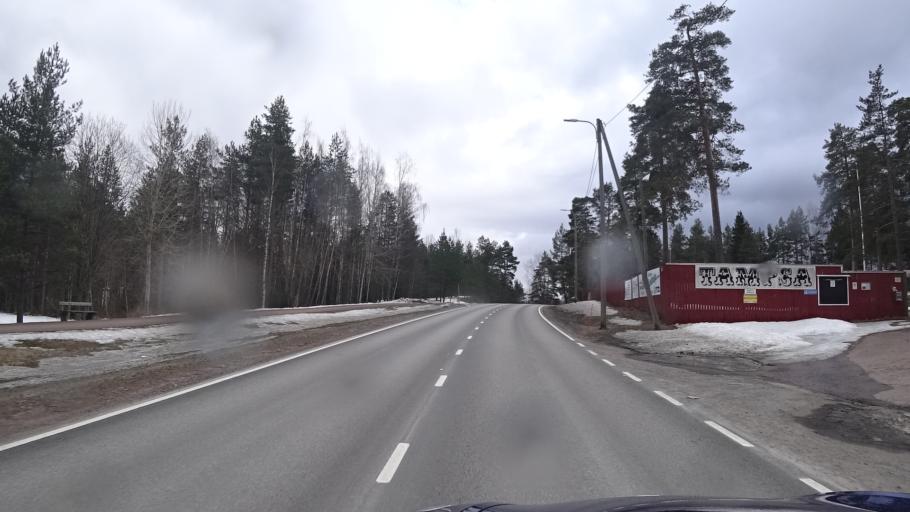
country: FI
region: Kymenlaakso
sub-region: Kotka-Hamina
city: Karhula
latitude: 60.5230
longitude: 26.9004
